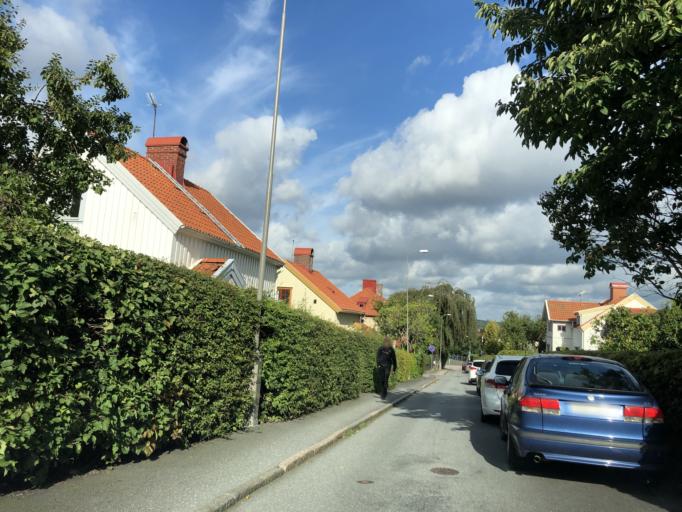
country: SE
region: Vaestra Goetaland
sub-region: Goteborg
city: Goeteborg
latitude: 57.7198
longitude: 12.0112
